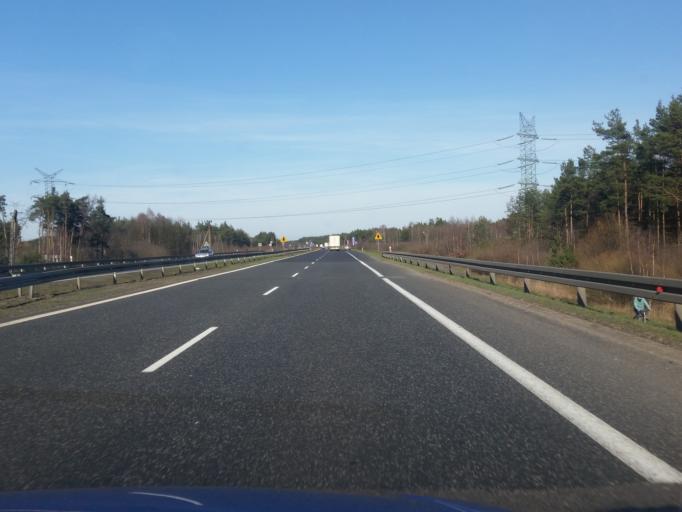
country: PL
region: Silesian Voivodeship
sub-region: Powiat czestochowski
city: Borowno
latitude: 51.0283
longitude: 19.3282
